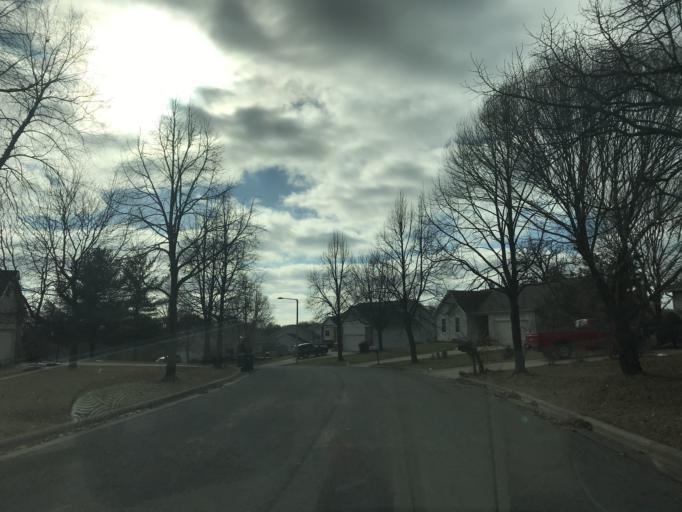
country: US
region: Wisconsin
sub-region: Dane County
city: Monona
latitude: 43.1164
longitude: -89.3003
